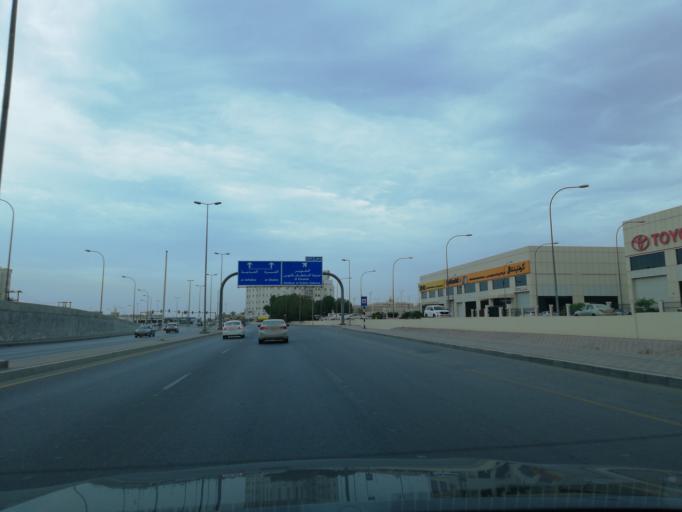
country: OM
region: Muhafazat Masqat
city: Bawshar
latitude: 23.5729
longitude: 58.3819
